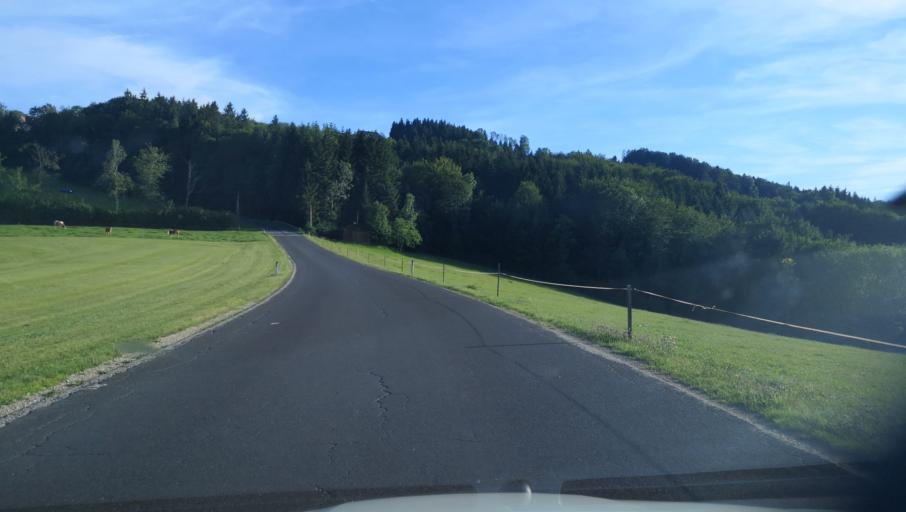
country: AT
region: Lower Austria
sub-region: Politischer Bezirk Amstetten
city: Neuhofen an der Ybbs
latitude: 48.0007
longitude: 14.8727
